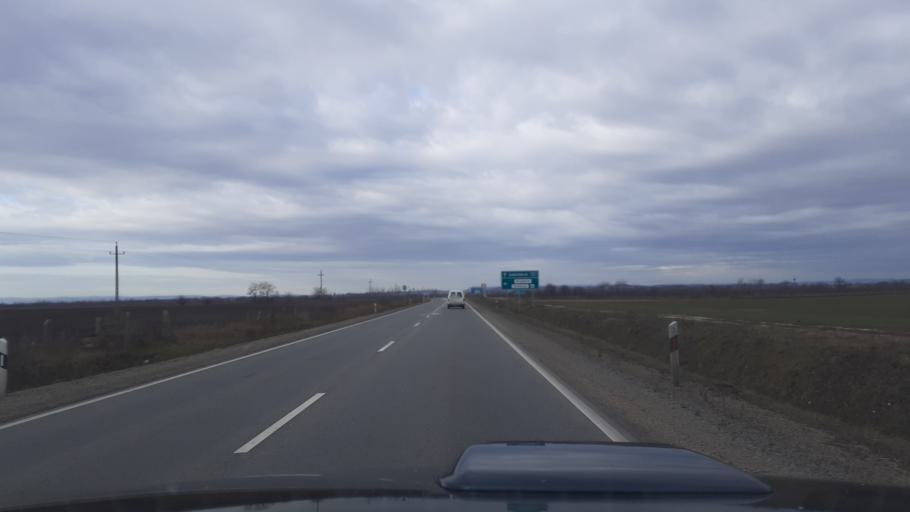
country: HU
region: Fejer
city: Seregelyes
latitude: 47.1485
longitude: 18.5245
